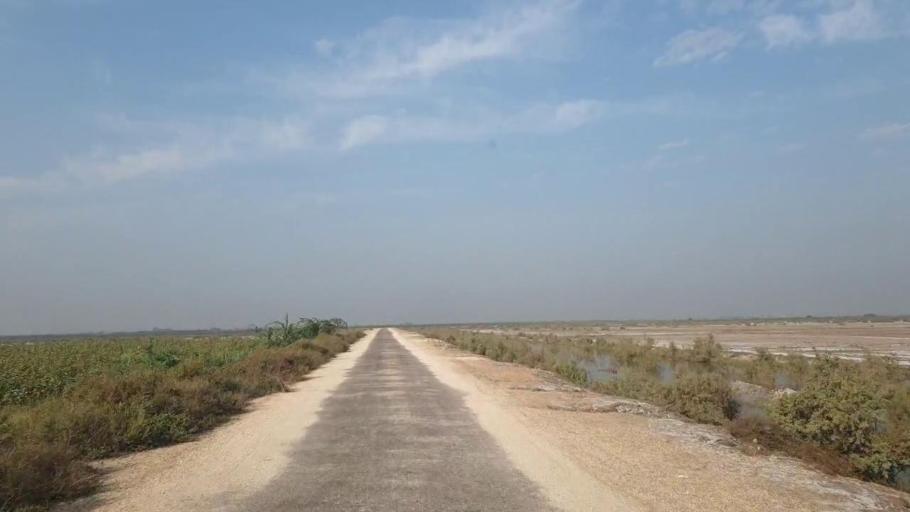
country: PK
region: Sindh
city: Tando Bago
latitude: 24.8446
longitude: 68.9893
